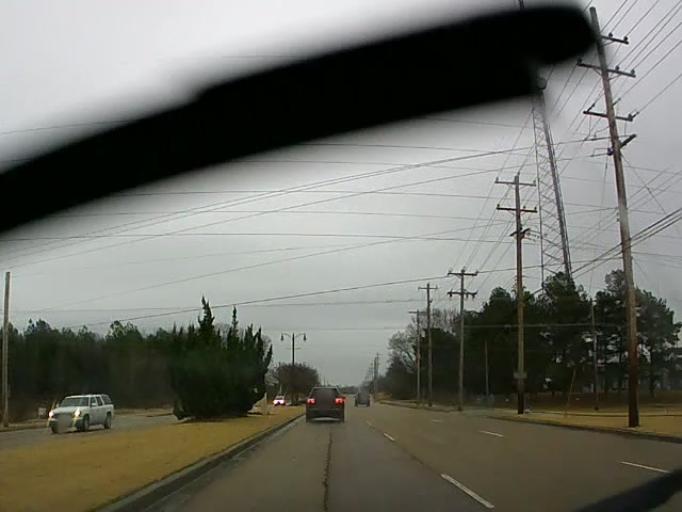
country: US
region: Tennessee
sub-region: Shelby County
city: Collierville
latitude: 35.0472
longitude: -89.7420
